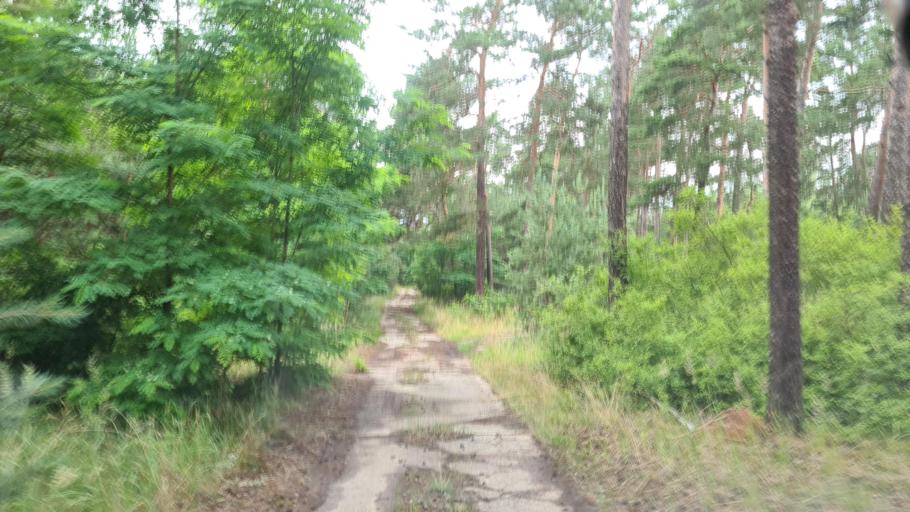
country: DE
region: Brandenburg
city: Crinitz
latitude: 51.7170
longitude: 13.7378
